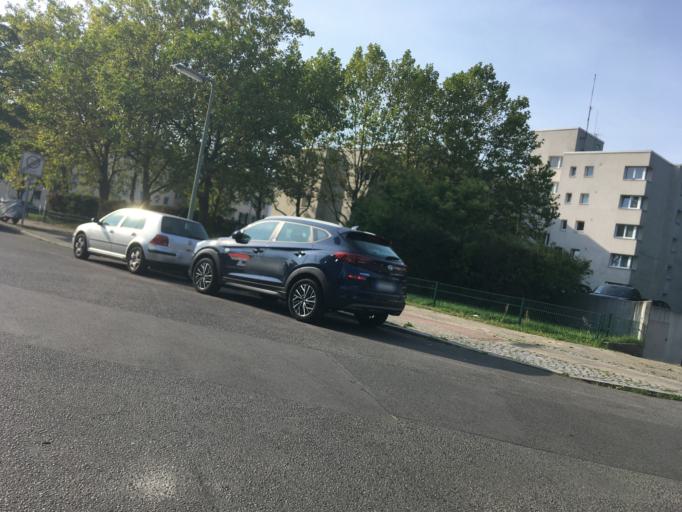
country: DE
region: Berlin
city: Buckow
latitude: 52.4276
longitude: 13.4464
